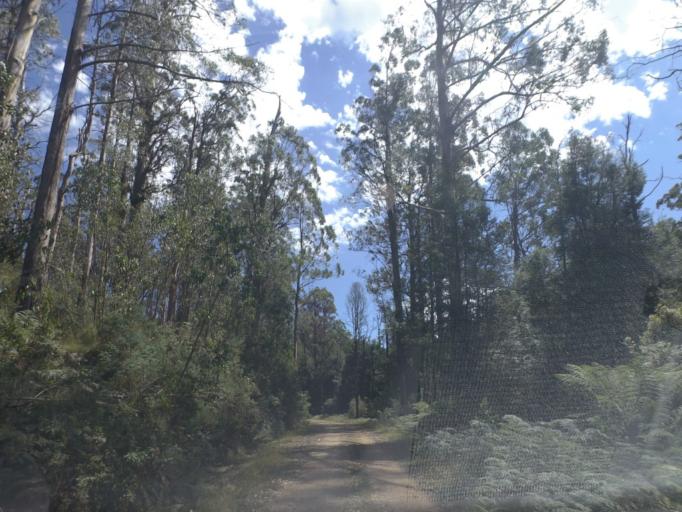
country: AU
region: Victoria
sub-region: Murrindindi
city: Alexandra
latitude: -37.4776
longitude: 145.8240
